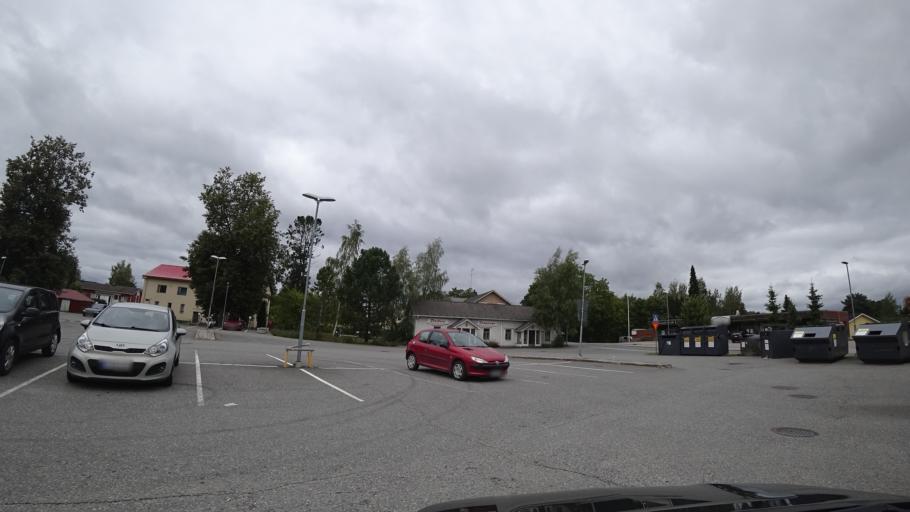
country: FI
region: Haeme
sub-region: Haemeenlinna
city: Lammi
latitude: 61.0797
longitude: 25.0110
